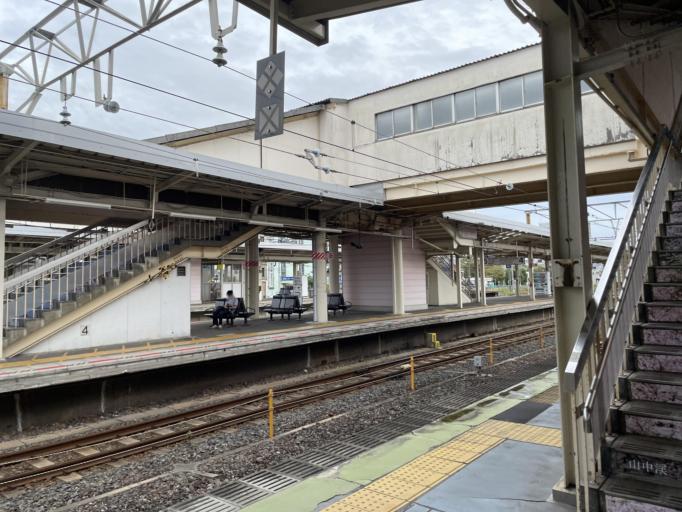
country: JP
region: Wakayama
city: Wakayama-shi
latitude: 34.2320
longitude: 135.1914
